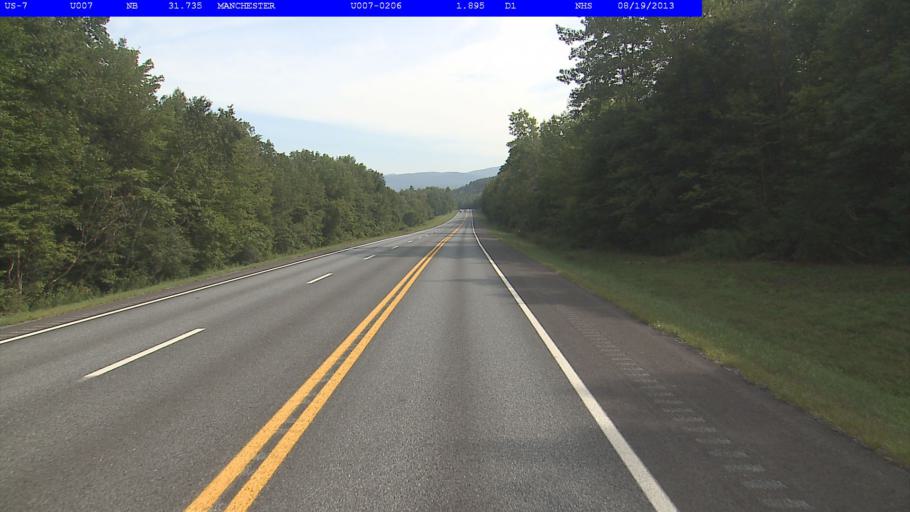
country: US
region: Vermont
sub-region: Bennington County
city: Manchester Center
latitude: 43.1395
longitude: -73.0578
